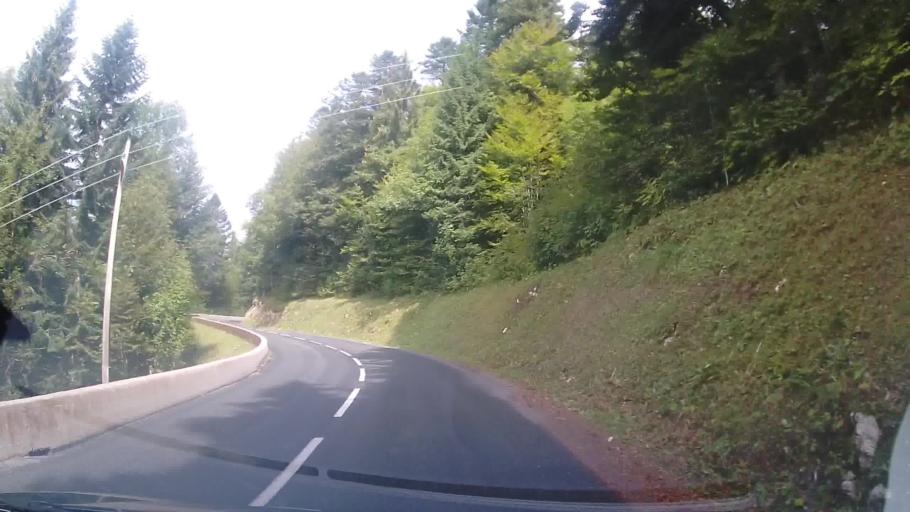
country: FR
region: Rhone-Alpes
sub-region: Departement de l'Ain
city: Gex
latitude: 46.3852
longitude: 6.0429
